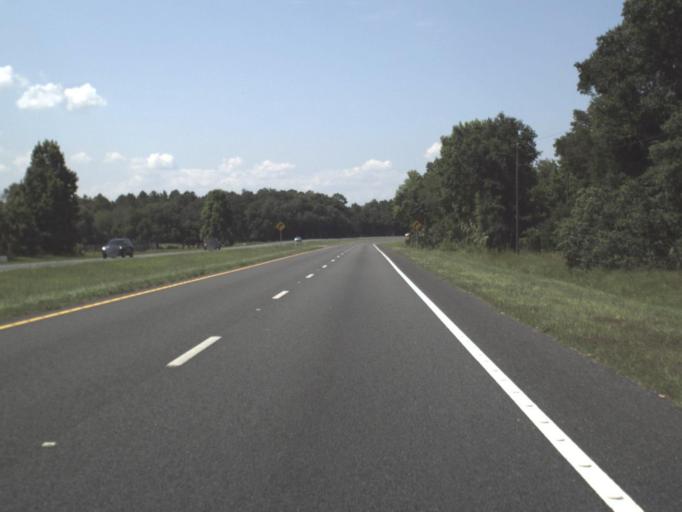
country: US
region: Florida
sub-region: Marion County
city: Citra
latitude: 29.4592
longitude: -82.1093
